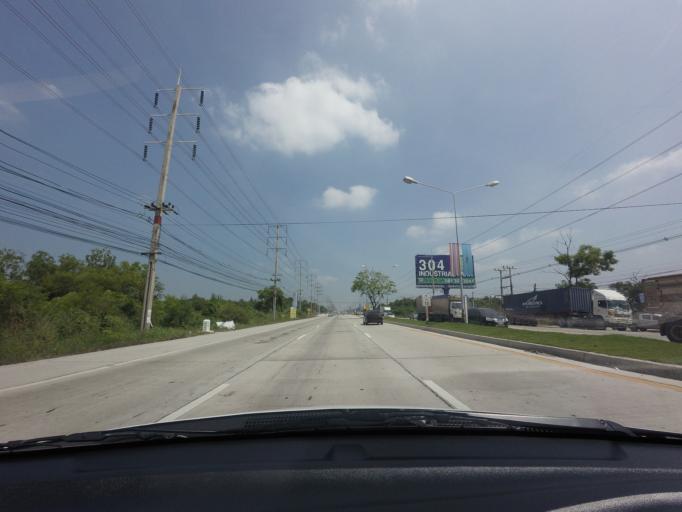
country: TH
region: Chachoengsao
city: Ban Pho
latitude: 13.6083
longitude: 101.0236
